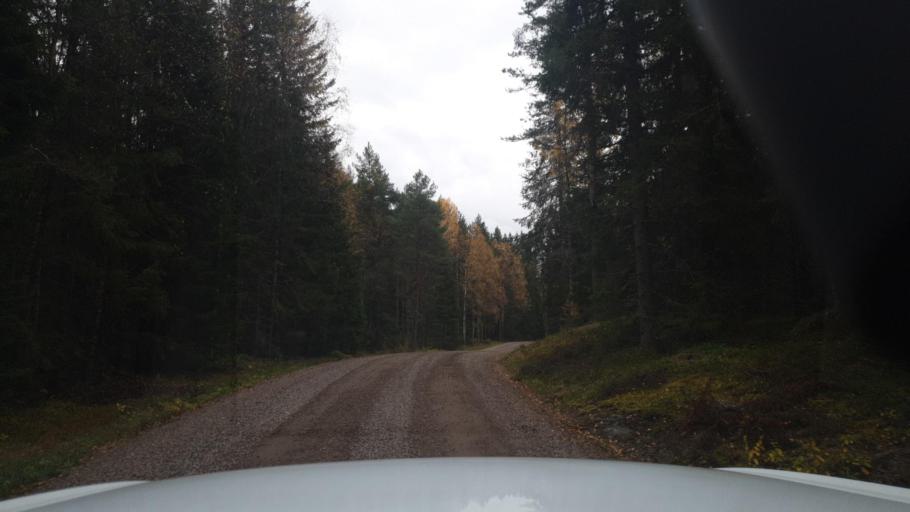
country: SE
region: Vaermland
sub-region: Arvika Kommun
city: Arvika
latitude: 59.9804
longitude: 12.6603
